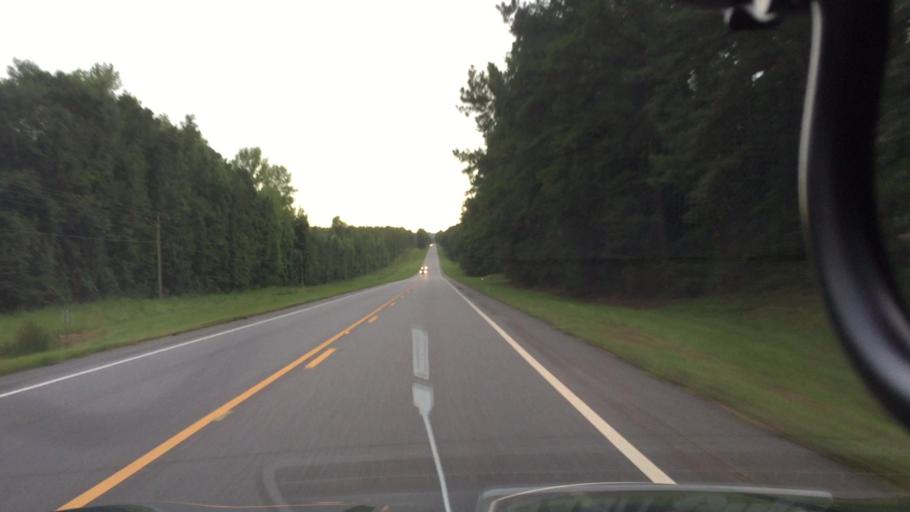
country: US
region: Alabama
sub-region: Coffee County
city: New Brockton
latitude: 31.5152
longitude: -85.9169
